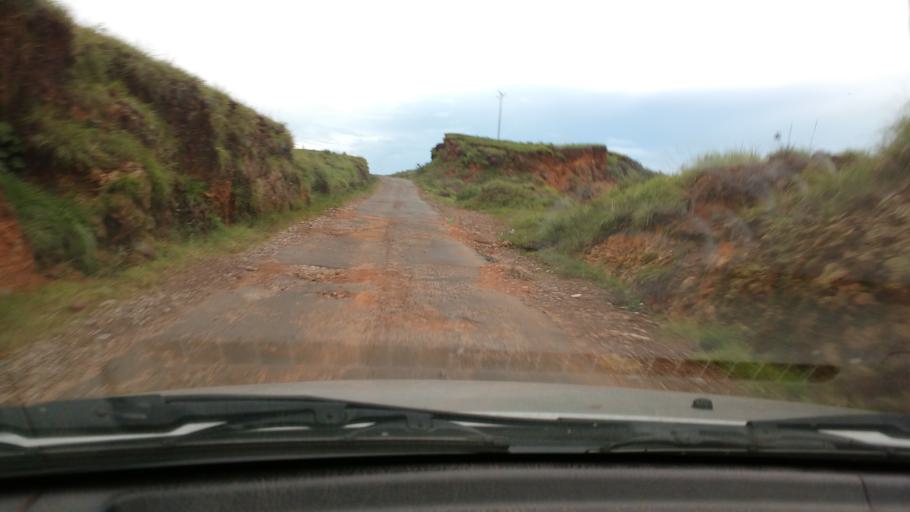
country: IN
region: Meghalaya
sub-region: East Khasi Hills
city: Cherrapunji
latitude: 25.2815
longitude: 91.7009
